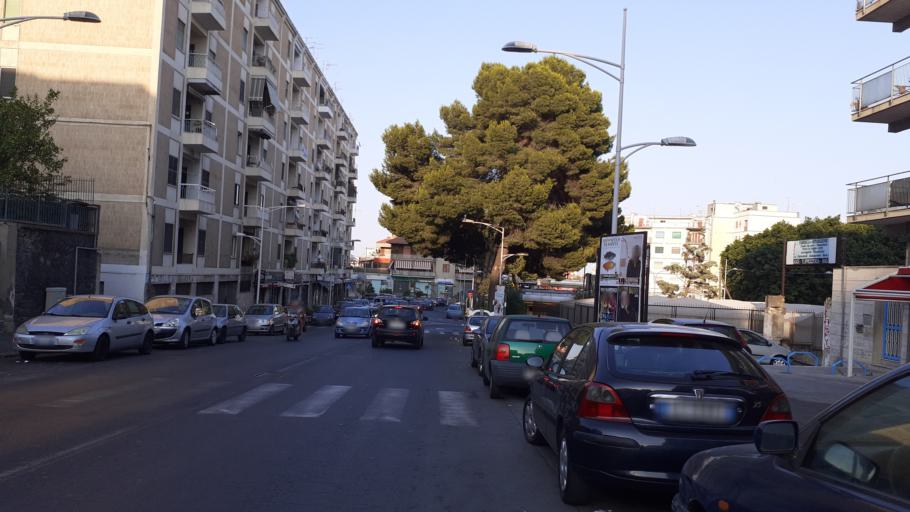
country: IT
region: Sicily
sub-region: Catania
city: Catania
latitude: 37.5015
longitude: 15.0690
